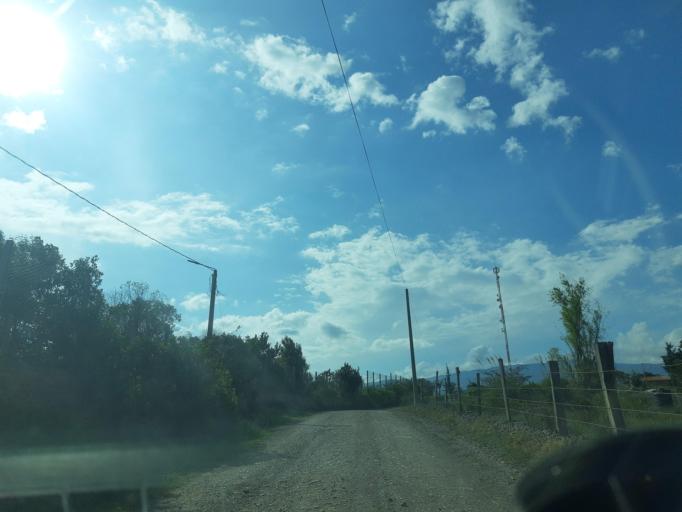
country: CO
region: Boyaca
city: Villa de Leiva
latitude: 5.6596
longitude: -73.5464
